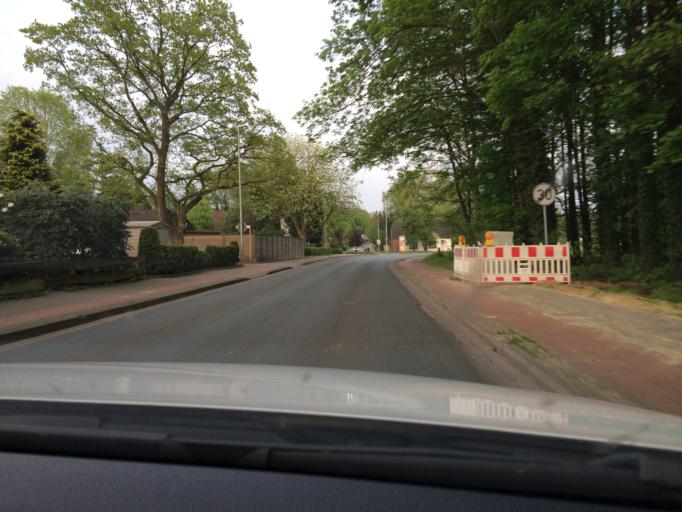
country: DE
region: Lower Saxony
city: Ganderkesee
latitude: 53.0305
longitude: 8.5544
